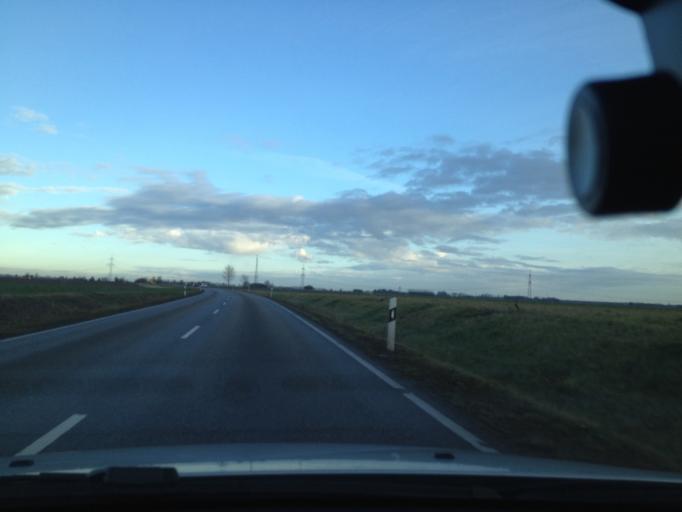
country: DE
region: Bavaria
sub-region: Swabia
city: Langerringen
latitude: 48.1663
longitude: 10.7669
